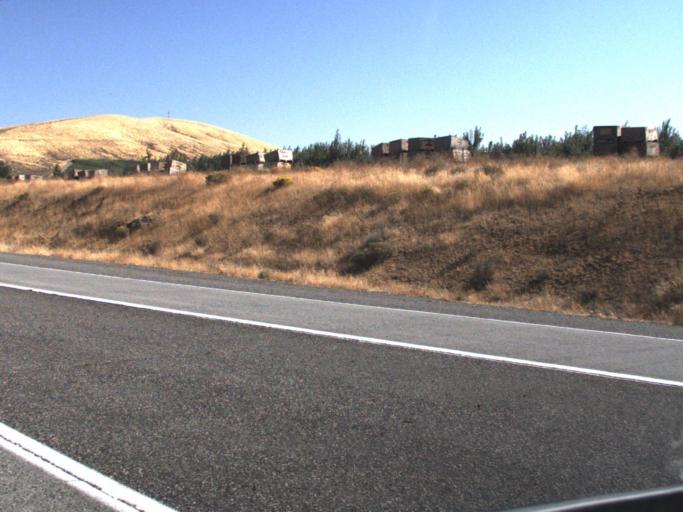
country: US
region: Washington
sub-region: Benton County
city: West Richland
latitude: 46.2444
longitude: -119.3575
